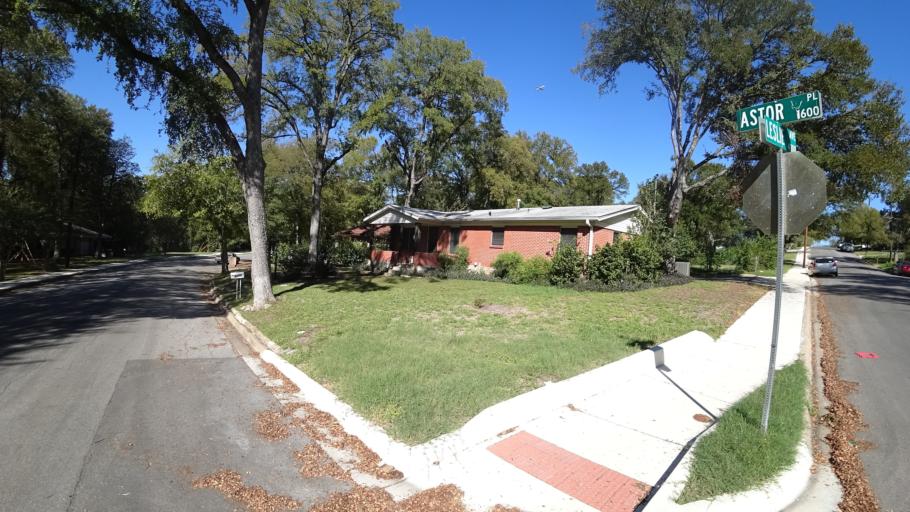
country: US
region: Texas
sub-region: Travis County
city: Austin
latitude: 30.2824
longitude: -97.6883
